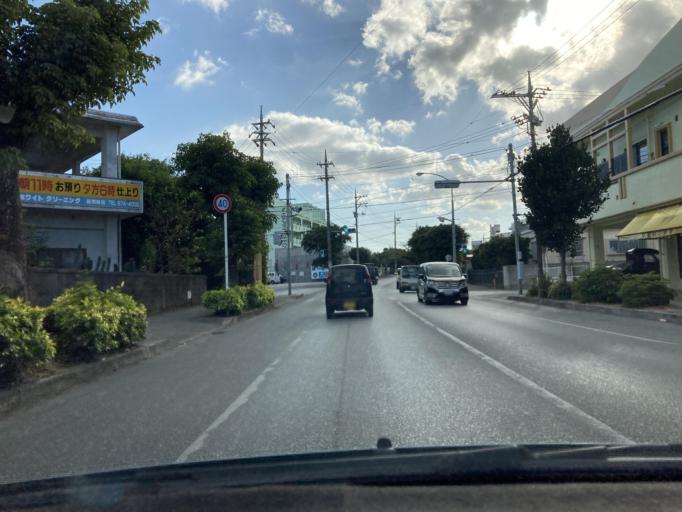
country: JP
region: Okinawa
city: Gushikawa
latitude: 26.3605
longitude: 127.8514
